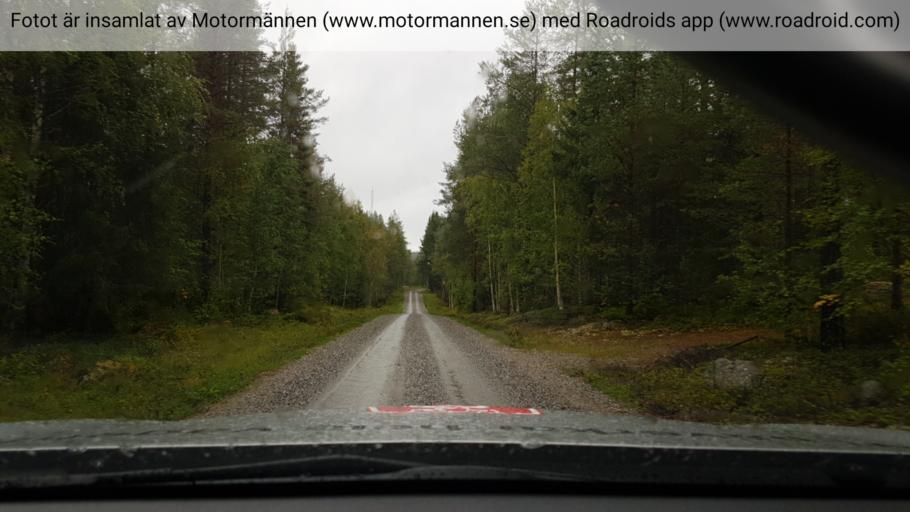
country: SE
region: Vaesterbotten
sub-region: Asele Kommun
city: Asele
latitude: 63.9795
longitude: 17.5792
